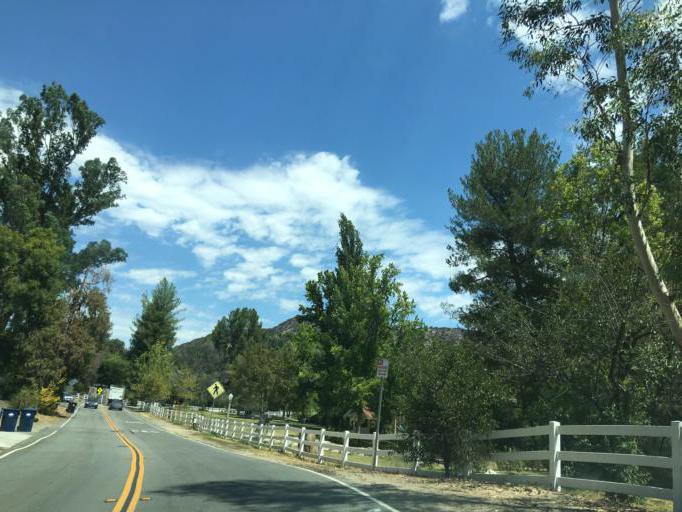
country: US
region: California
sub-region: Los Angeles County
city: Agoura Hills
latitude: 34.1080
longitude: -118.7561
